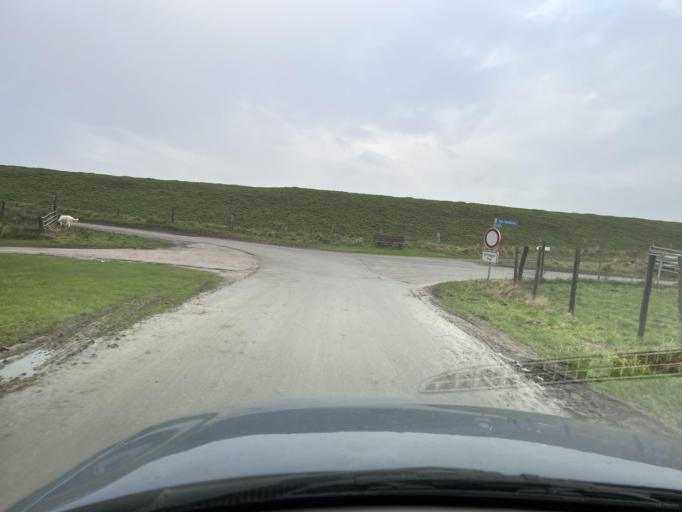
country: DE
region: Schleswig-Holstein
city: Hellschen-Heringsand-Unterschaar
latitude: 54.2219
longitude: 8.8574
